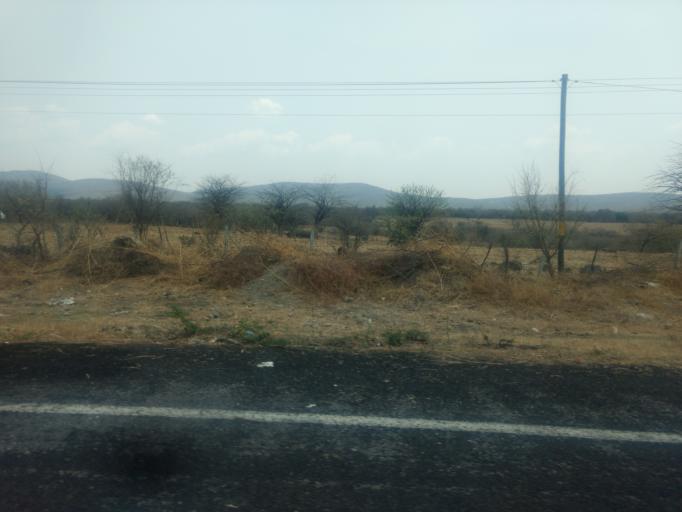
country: MX
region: Morelos
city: La Joya
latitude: 18.6720
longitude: -99.4332
